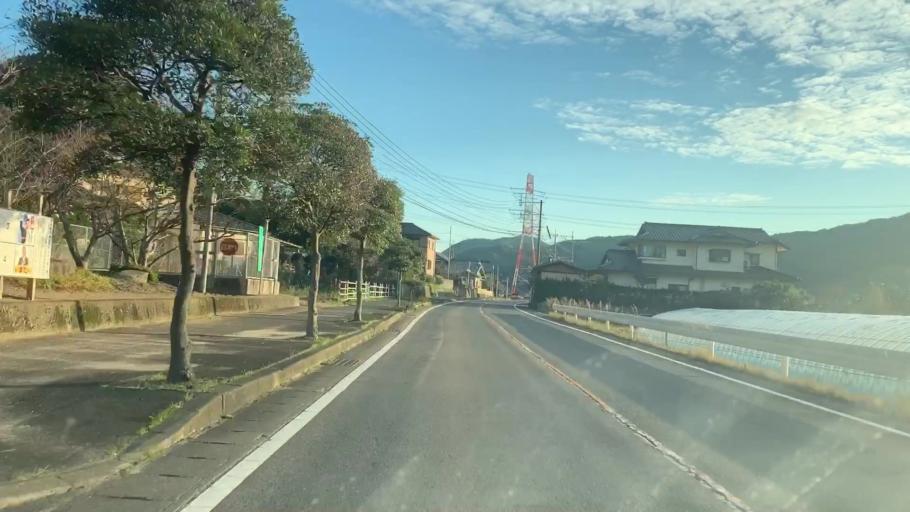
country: JP
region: Saga Prefecture
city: Karatsu
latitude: 33.3900
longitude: 129.9875
